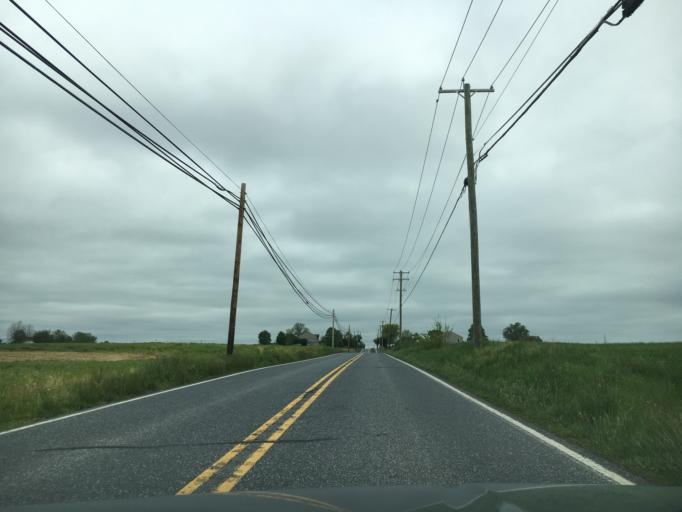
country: US
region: Pennsylvania
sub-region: Berks County
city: Fleetwood
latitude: 40.4809
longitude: -75.8341
